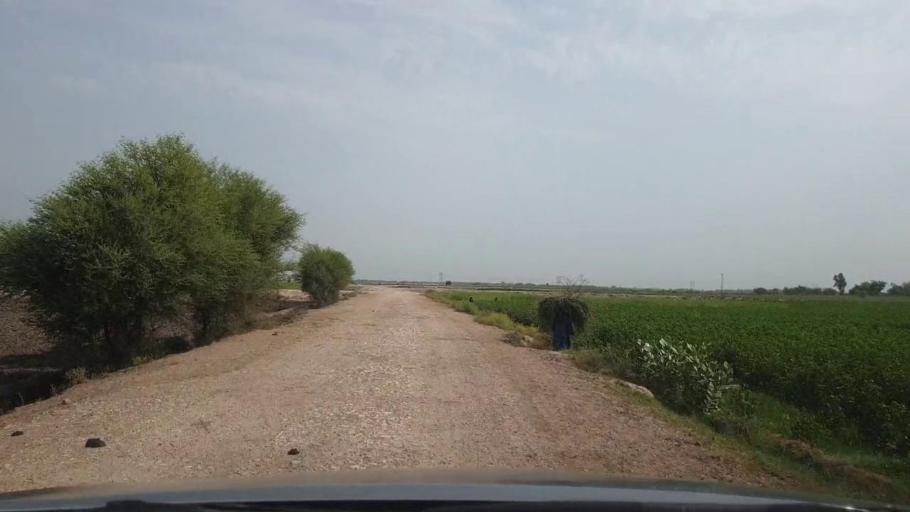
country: PK
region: Sindh
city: Rohri
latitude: 27.6603
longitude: 69.0254
